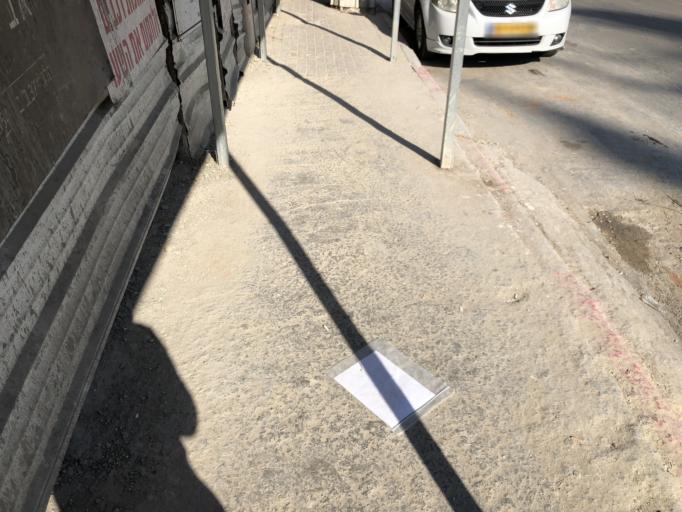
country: IL
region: Tel Aviv
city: Giv`atayim
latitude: 32.0696
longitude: 34.8124
